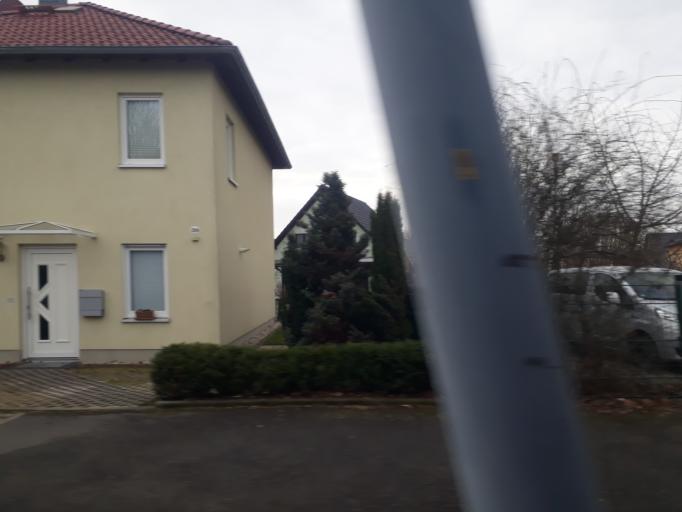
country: DE
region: Saxony
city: Heidenau
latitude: 51.0093
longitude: 13.8356
